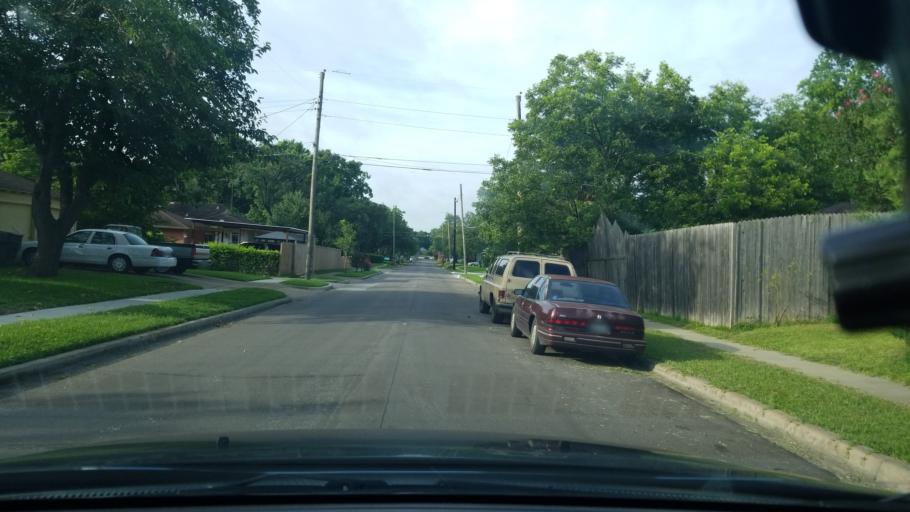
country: US
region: Texas
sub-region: Dallas County
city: Garland
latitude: 32.8304
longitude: -96.6606
